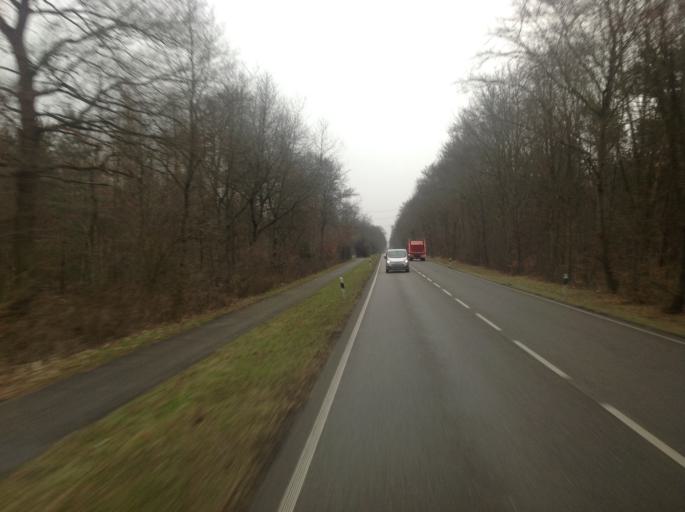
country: DE
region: Baden-Wuerttemberg
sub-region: Karlsruhe Region
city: Iffezheim
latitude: 48.8274
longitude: 8.1693
